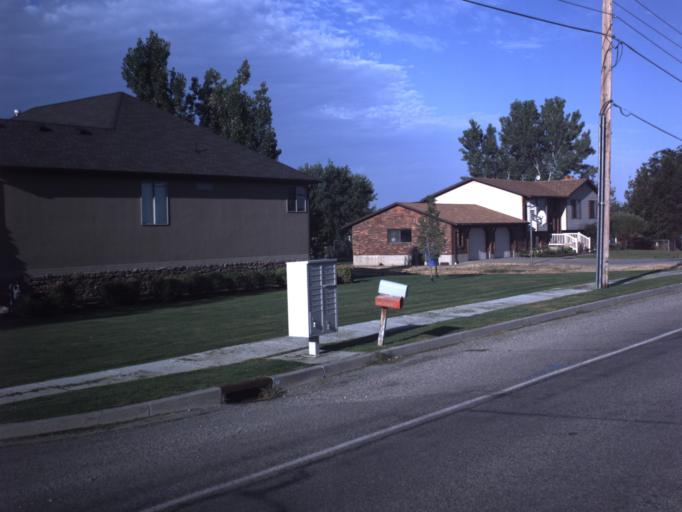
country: US
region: Utah
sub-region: Weber County
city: Plain City
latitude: 41.3050
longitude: -112.0601
